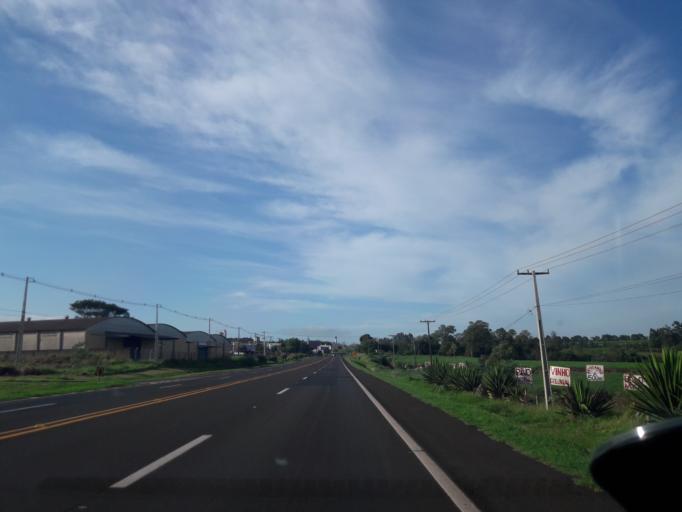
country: BR
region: Parana
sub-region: Arapongas
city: Arapongas
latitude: -23.3954
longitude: -51.4614
